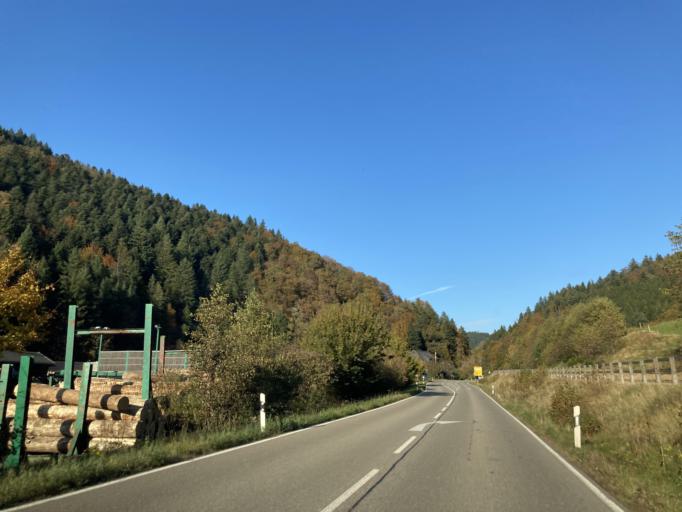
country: DE
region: Baden-Wuerttemberg
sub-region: Freiburg Region
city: Buchenbach
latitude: 47.9710
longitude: 8.0318
